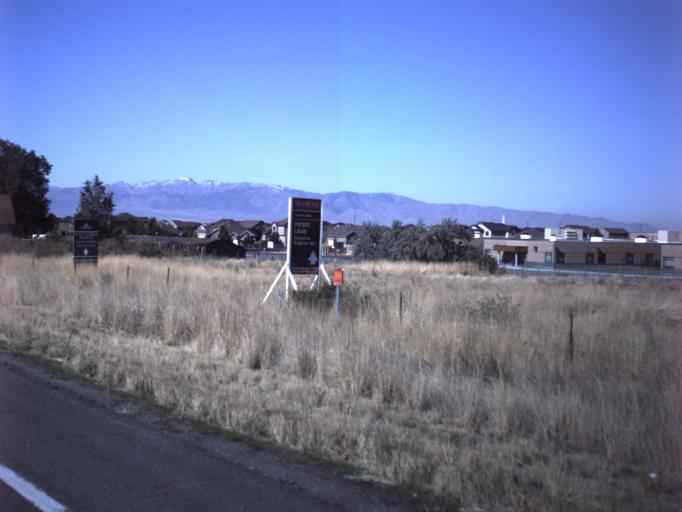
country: US
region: Utah
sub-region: Tooele County
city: Stansbury park
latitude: 40.6495
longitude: -112.2985
